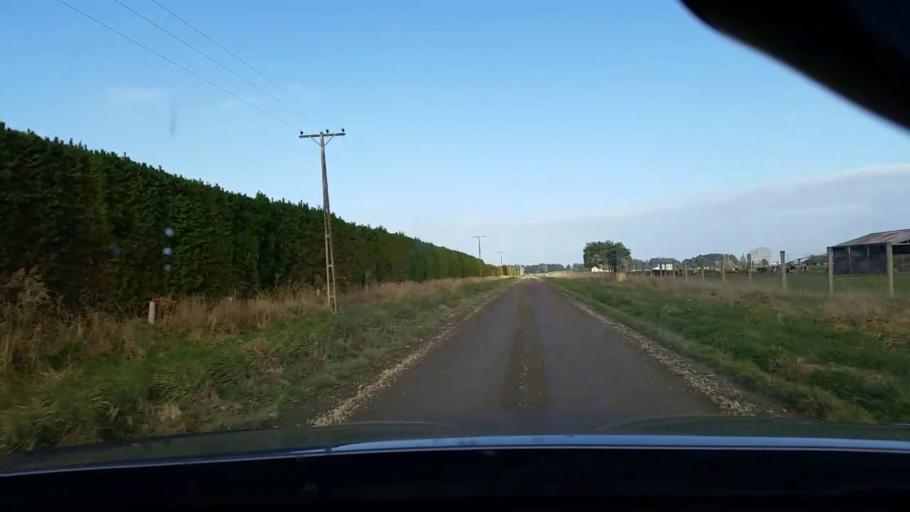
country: NZ
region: Southland
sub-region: Invercargill City
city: Invercargill
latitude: -46.2857
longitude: 168.2947
